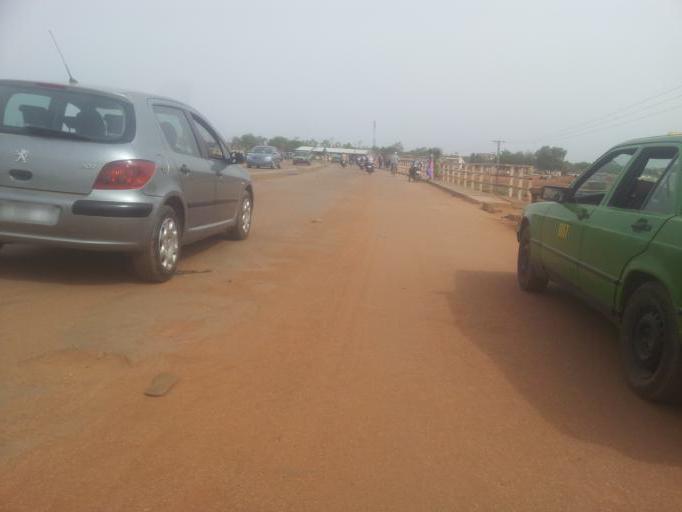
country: BF
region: Centre
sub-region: Kadiogo Province
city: Ouagadougou
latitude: 12.3841
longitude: -1.5538
